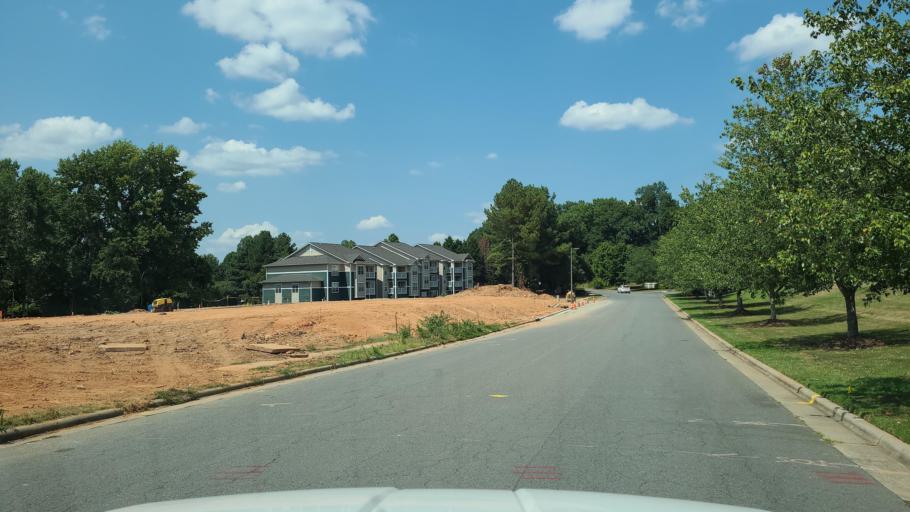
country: US
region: North Carolina
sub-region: Iredell County
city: Mooresville
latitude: 35.5992
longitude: -80.8676
